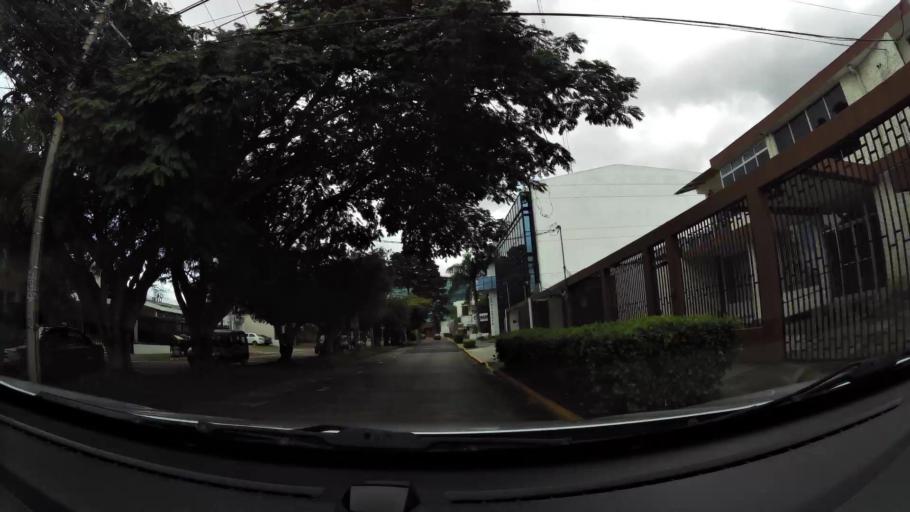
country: CR
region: San Jose
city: San Pedro
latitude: 9.9334
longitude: -84.0596
